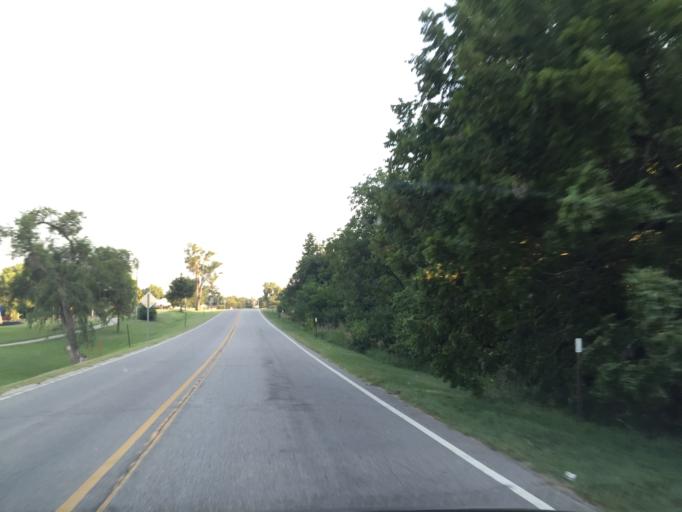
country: US
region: Kansas
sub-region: Ellsworth County
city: Ellsworth
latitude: 38.7391
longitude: -98.2252
